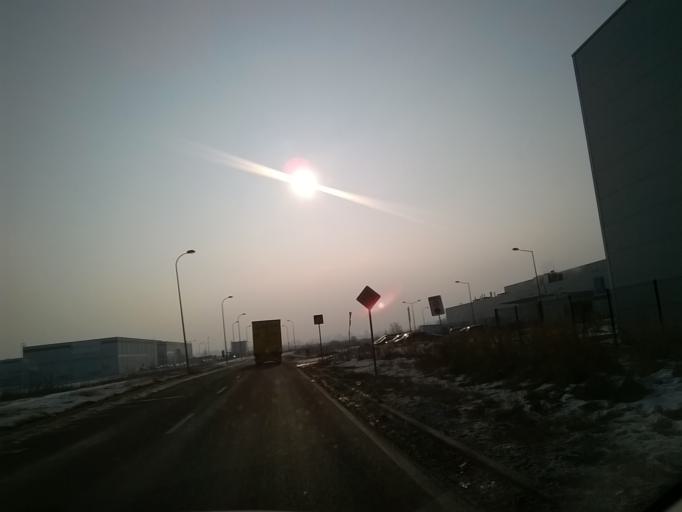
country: SK
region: Nitriansky
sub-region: Okres Nitra
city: Nitra
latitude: 48.3313
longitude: 18.0579
